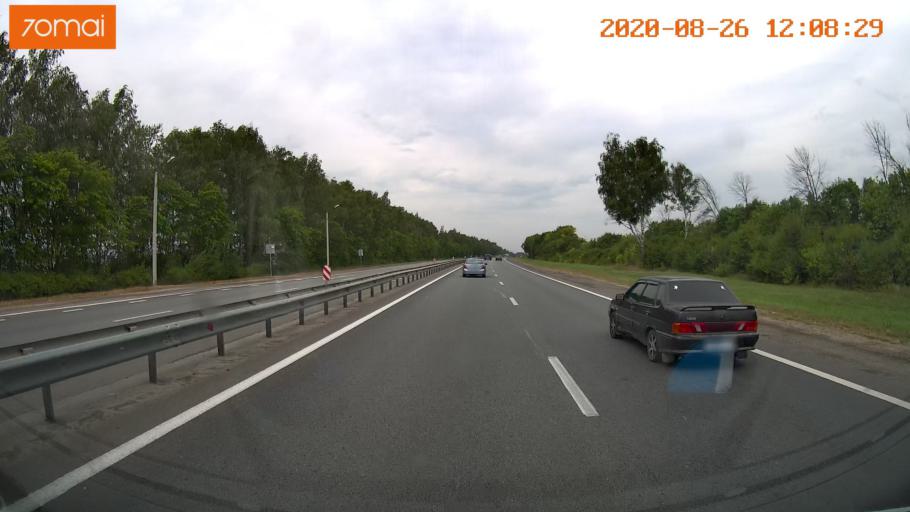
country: RU
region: Rjazan
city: Starozhilovo
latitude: 54.3519
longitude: 40.1189
